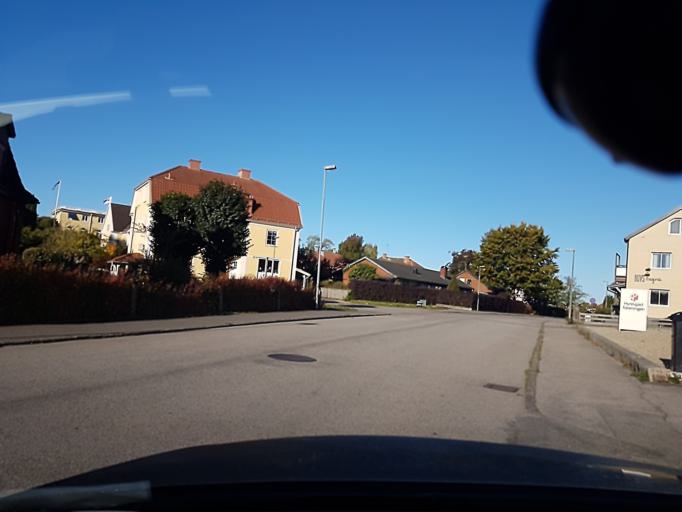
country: SE
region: Kronoberg
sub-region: Vaxjo Kommun
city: Vaexjoe
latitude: 56.8771
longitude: 14.8193
